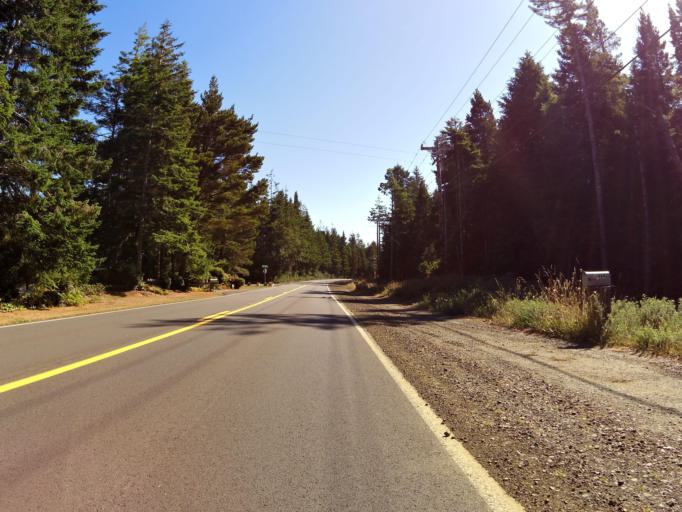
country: US
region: Oregon
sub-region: Coos County
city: Bandon
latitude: 43.2046
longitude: -124.3671
